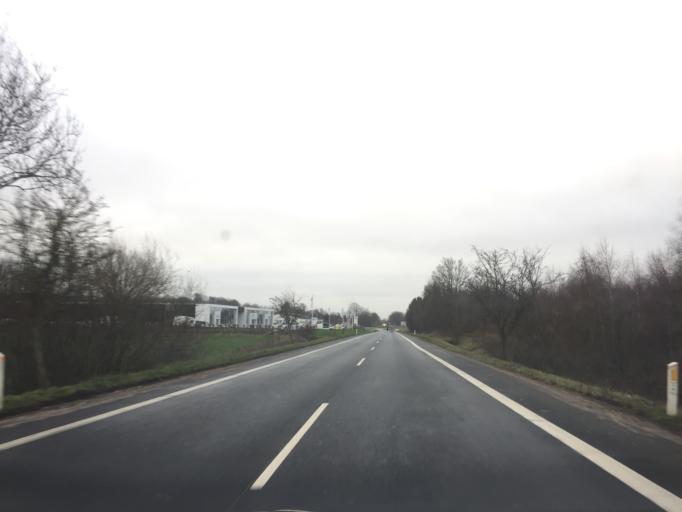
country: DK
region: South Denmark
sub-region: Svendborg Kommune
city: Svendborg
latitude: 55.0834
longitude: 10.6291
